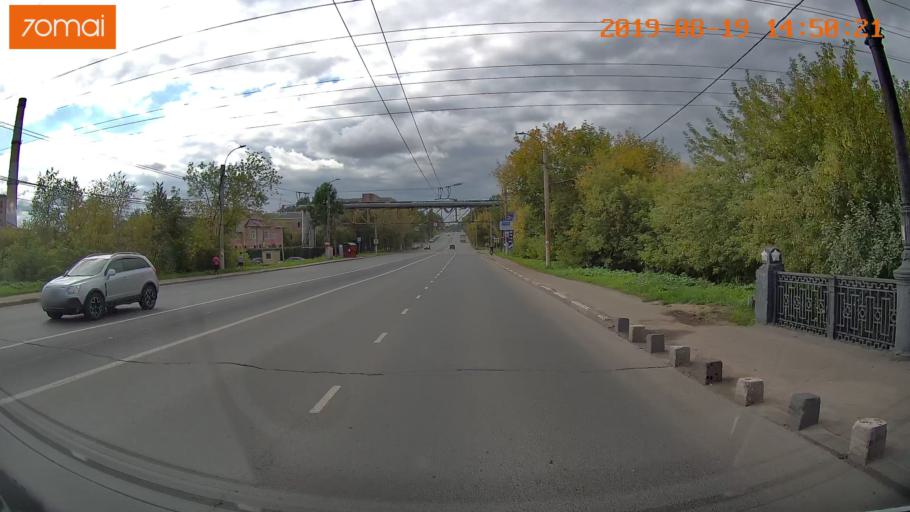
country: RU
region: Ivanovo
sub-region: Gorod Ivanovo
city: Ivanovo
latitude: 56.9938
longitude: 41.0157
